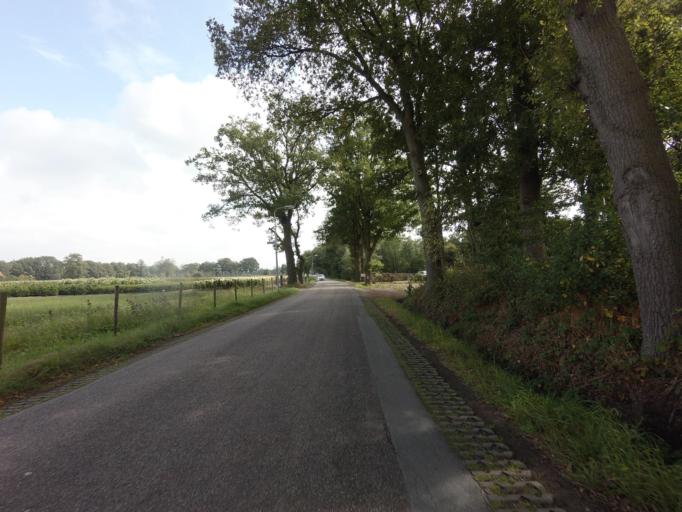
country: NL
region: Overijssel
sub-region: Gemeente Hengelo
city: Hengelo
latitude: 52.2747
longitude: 6.8286
